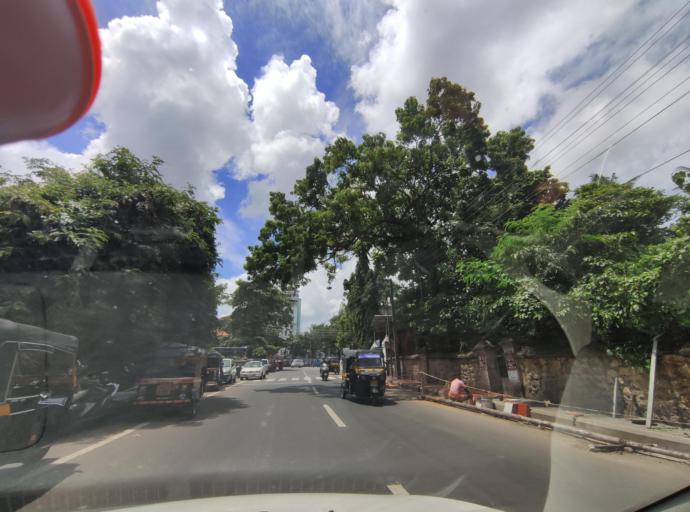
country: IN
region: Kerala
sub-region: Thiruvananthapuram
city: Thiruvananthapuram
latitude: 8.5088
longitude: 76.9484
